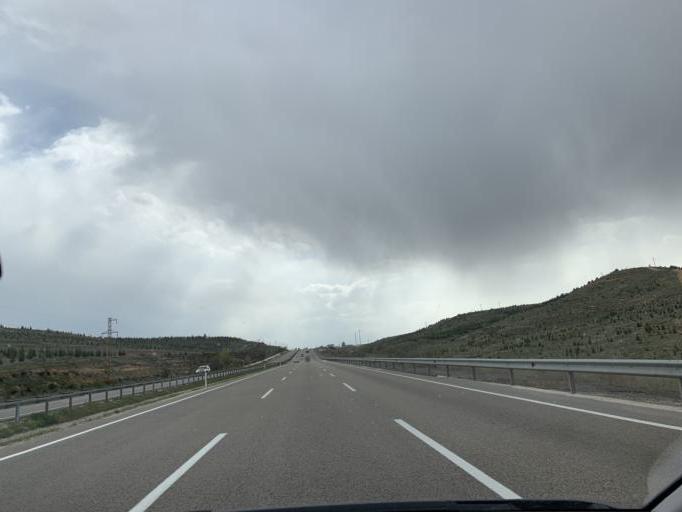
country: TR
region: Eskisehir
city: Sivrihisar
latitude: 39.5146
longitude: 31.6166
